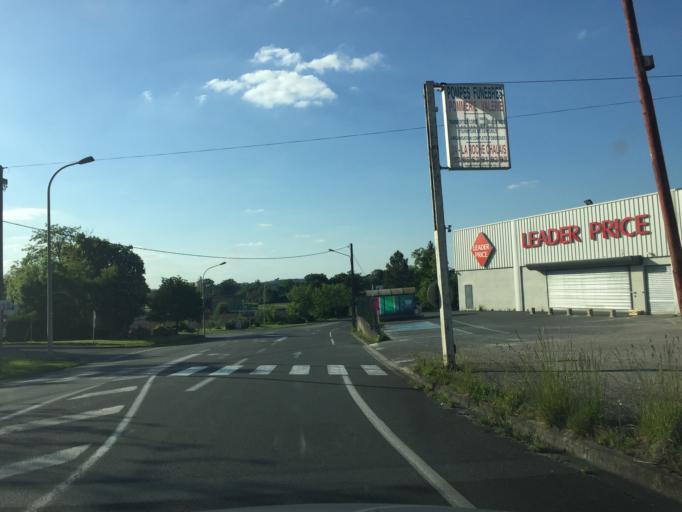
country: FR
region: Aquitaine
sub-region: Departement de la Dordogne
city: La Roche-Chalais
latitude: 45.1560
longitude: 0.0076
